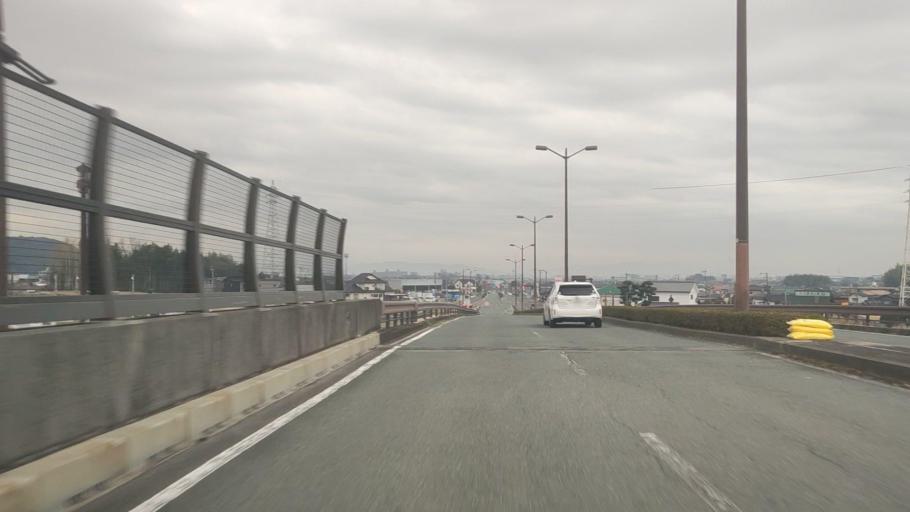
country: JP
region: Kumamoto
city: Ozu
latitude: 32.8358
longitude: 130.8022
